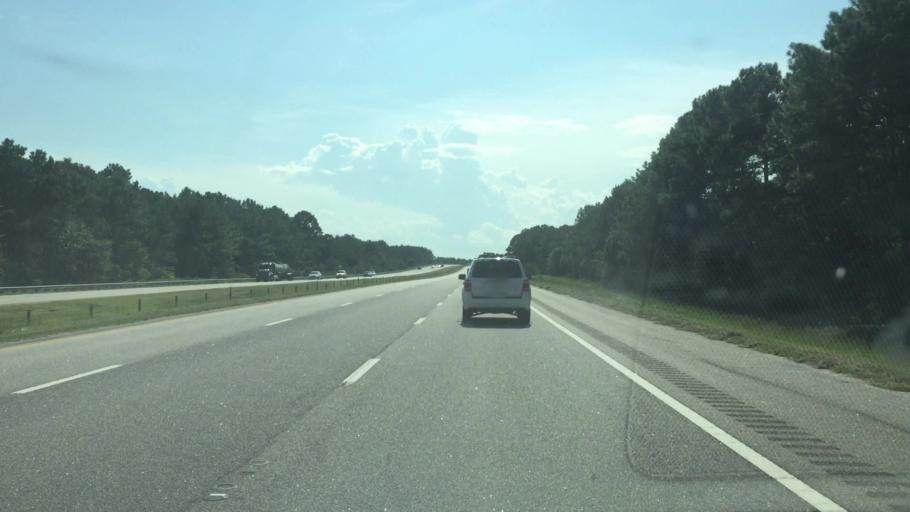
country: US
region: South Carolina
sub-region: Horry County
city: North Myrtle Beach
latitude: 33.8130
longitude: -78.7615
